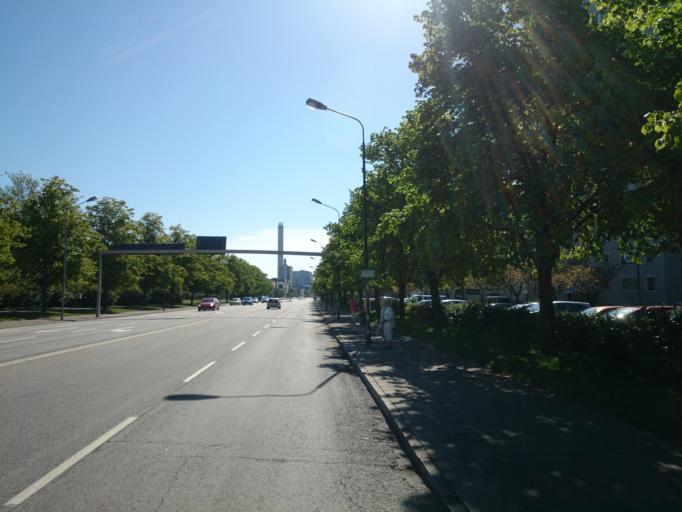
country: SE
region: Skane
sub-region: Malmo
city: Malmoe
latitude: 55.5799
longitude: 12.9971
